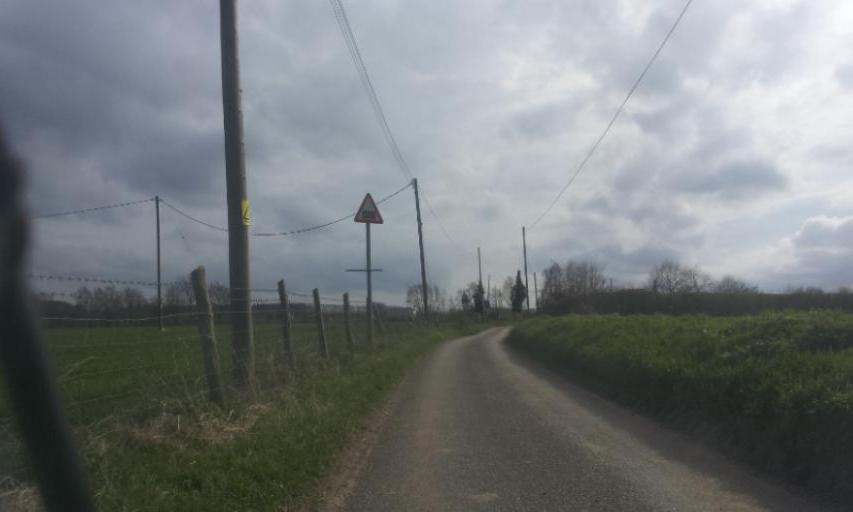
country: GB
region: England
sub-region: Kent
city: Teynham
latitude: 51.3243
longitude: 0.8396
